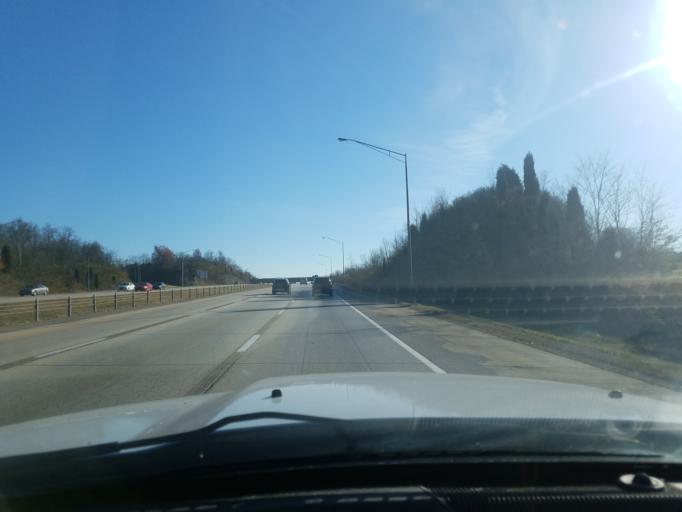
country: US
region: Kentucky
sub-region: Kenton County
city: Taylor Mill
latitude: 39.0228
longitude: -84.5171
